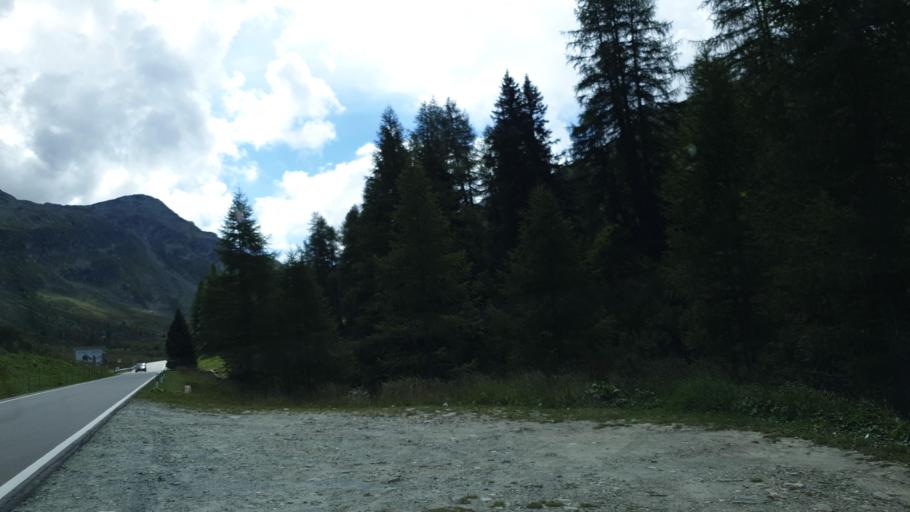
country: IT
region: Lombardy
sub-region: Provincia di Sondrio
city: Campodolcino
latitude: 46.5268
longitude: 9.3293
